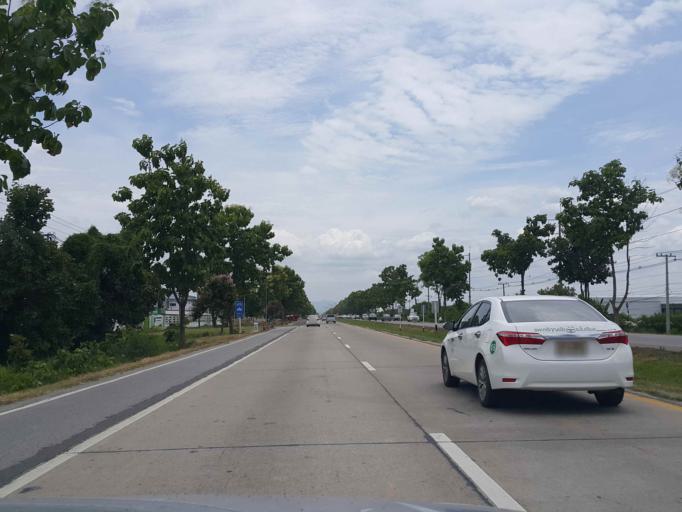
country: TH
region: Chiang Mai
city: Saraphi
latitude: 18.6774
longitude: 99.0509
